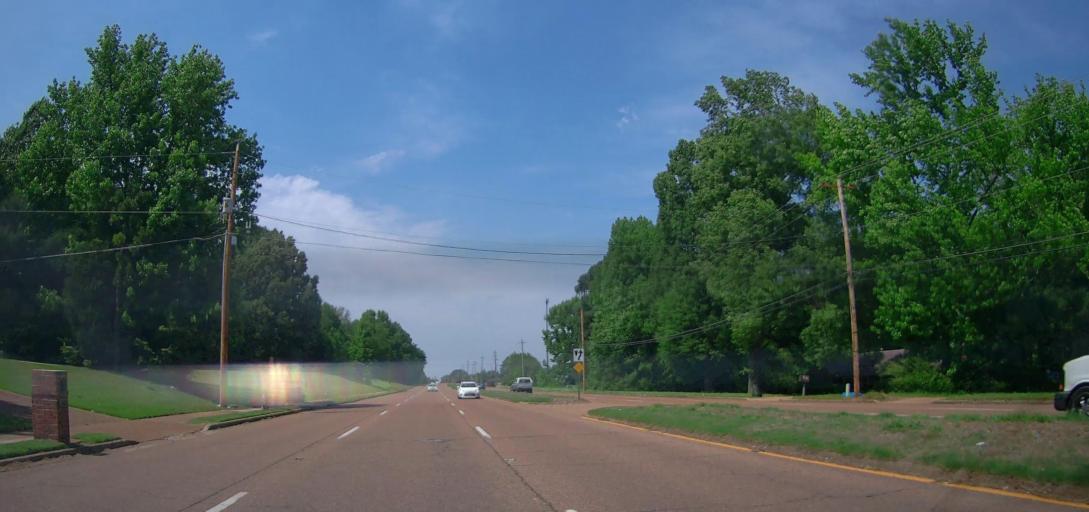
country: US
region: Mississippi
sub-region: De Soto County
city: Olive Branch
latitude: 35.0019
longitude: -89.8310
